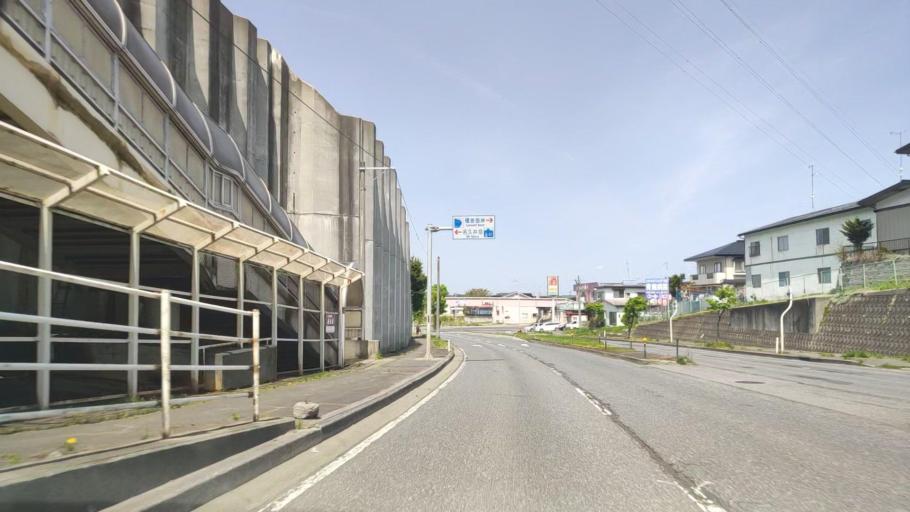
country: JP
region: Aomori
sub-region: Hachinohe Shi
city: Uchimaru
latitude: 40.5007
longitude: 141.4555
